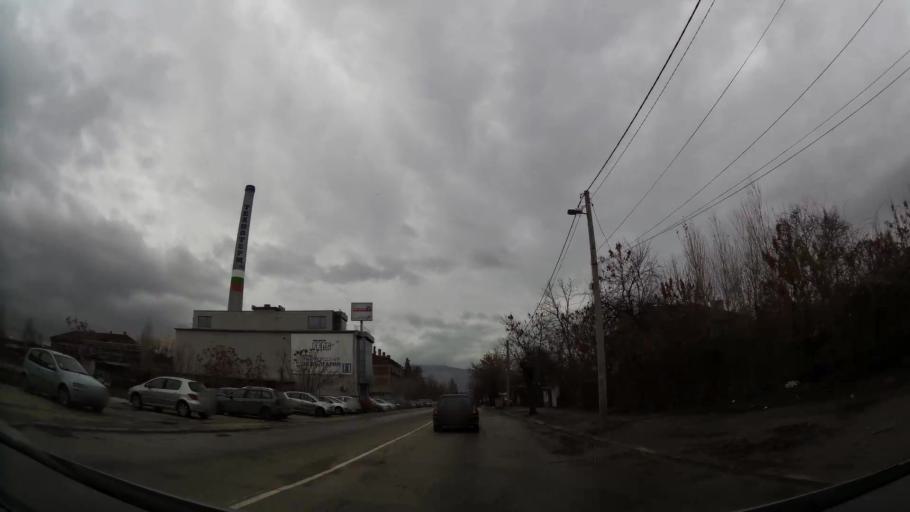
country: BG
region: Sofia-Capital
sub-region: Stolichna Obshtina
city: Sofia
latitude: 42.7240
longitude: 23.2812
